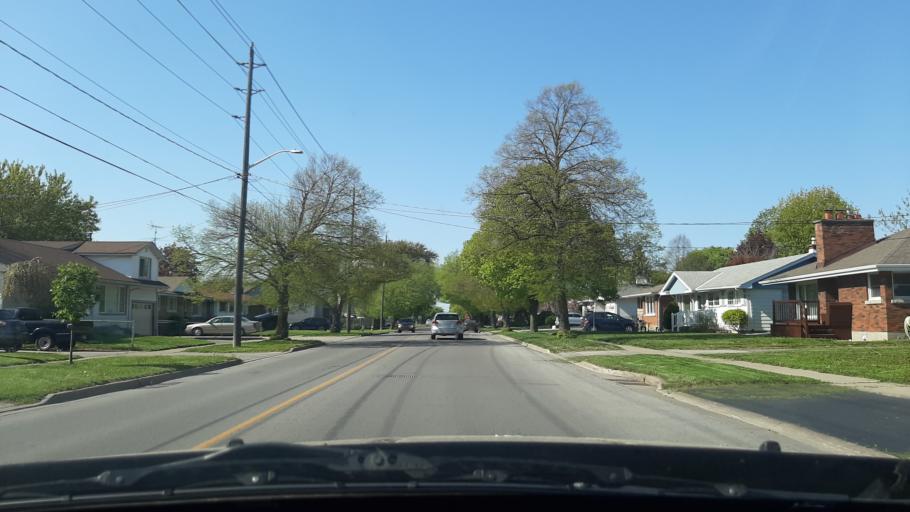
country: CA
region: Ontario
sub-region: Regional Municipality of Niagara
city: St. Catharines
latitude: 43.2034
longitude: -79.2115
